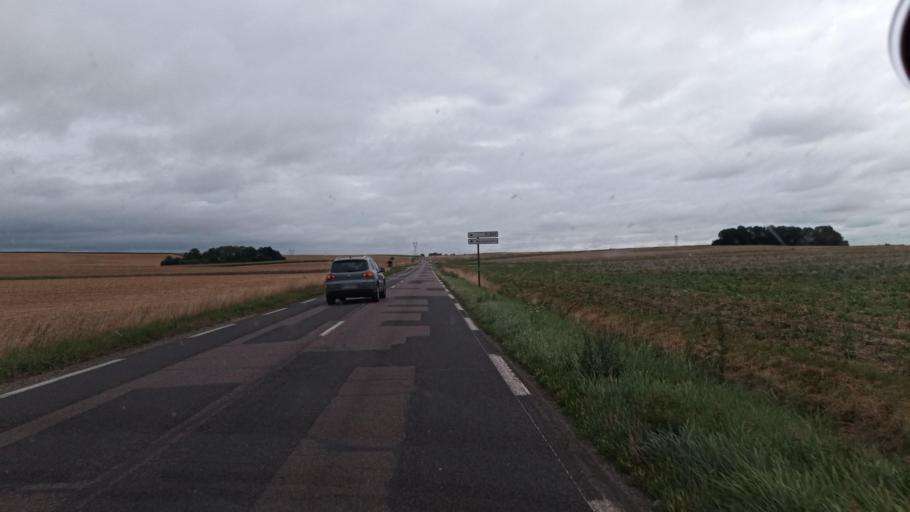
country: FR
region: Ile-de-France
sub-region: Departement de Seine-et-Marne
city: Voulx
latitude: 48.3191
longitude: 2.9509
